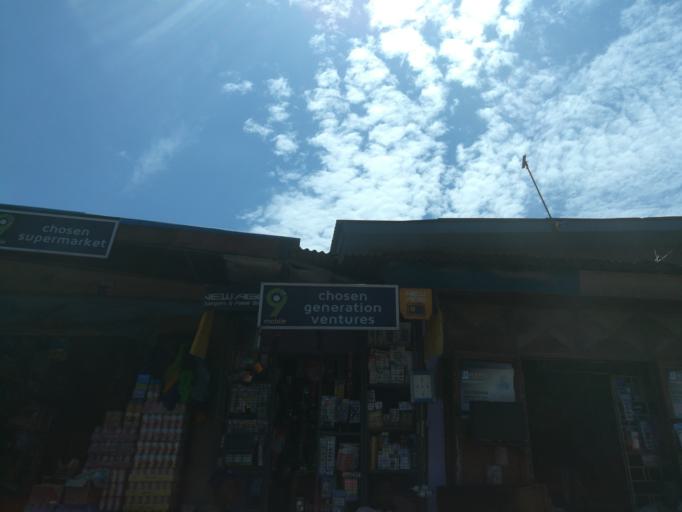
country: NG
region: Lagos
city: Oshodi
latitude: 6.5690
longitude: 3.3322
